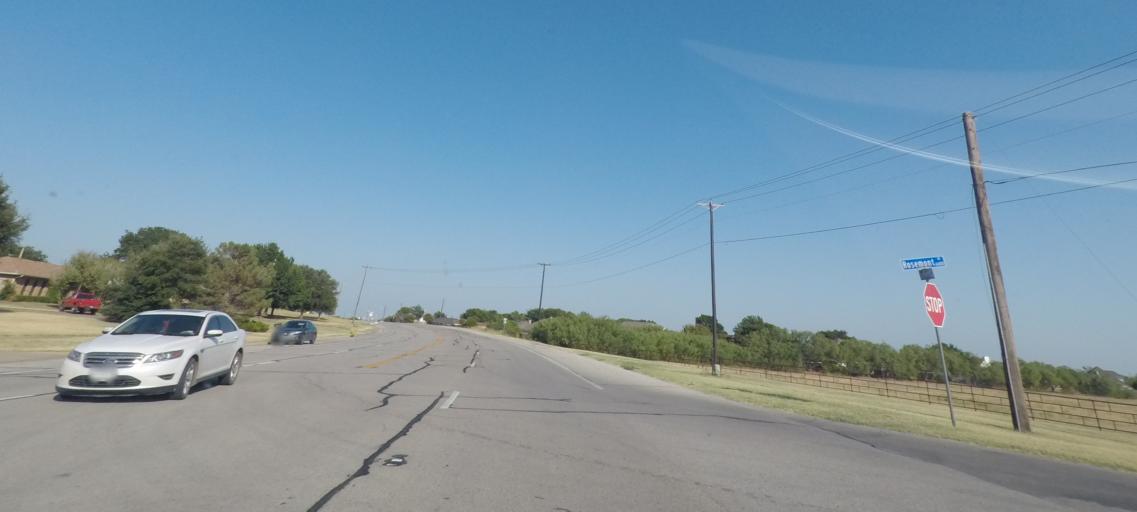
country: US
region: Texas
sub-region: Archer County
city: Holliday
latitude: 33.8598
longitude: -98.6000
